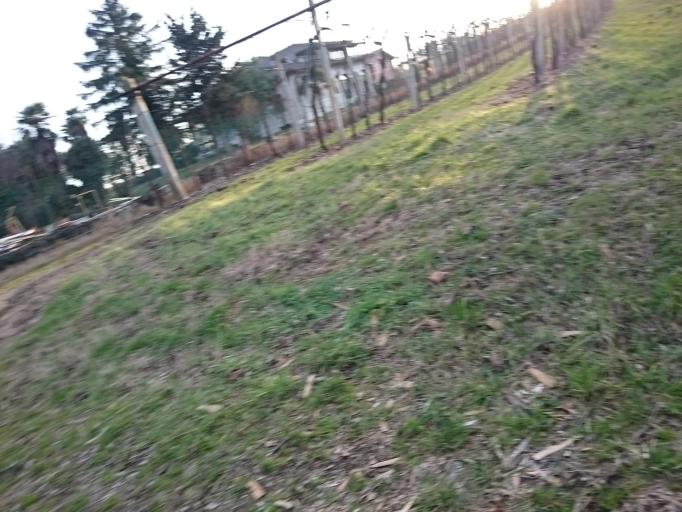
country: IT
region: Veneto
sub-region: Provincia di Verona
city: Castelnuovo del Garda
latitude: 45.4416
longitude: 10.7710
